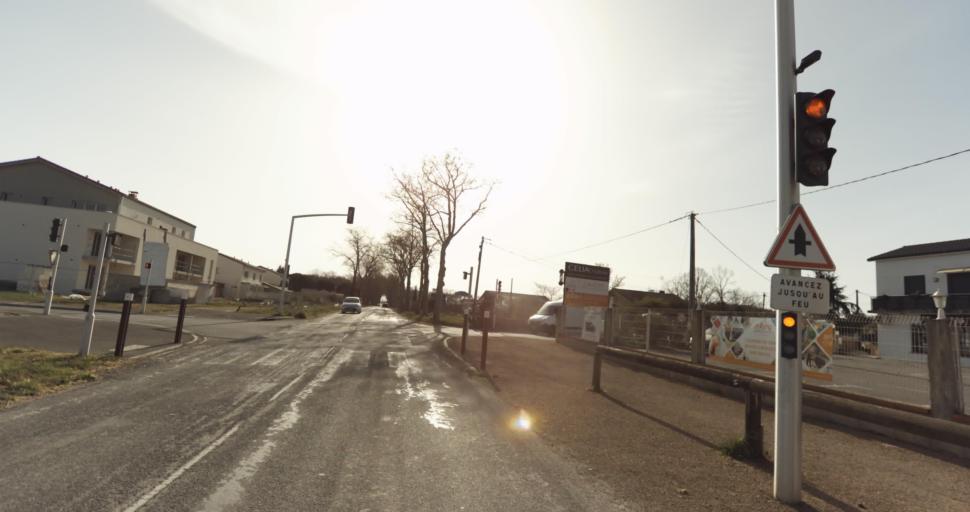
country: FR
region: Midi-Pyrenees
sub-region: Departement du Tarn
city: Saint-Sulpice-la-Pointe
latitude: 43.7615
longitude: 1.6985
